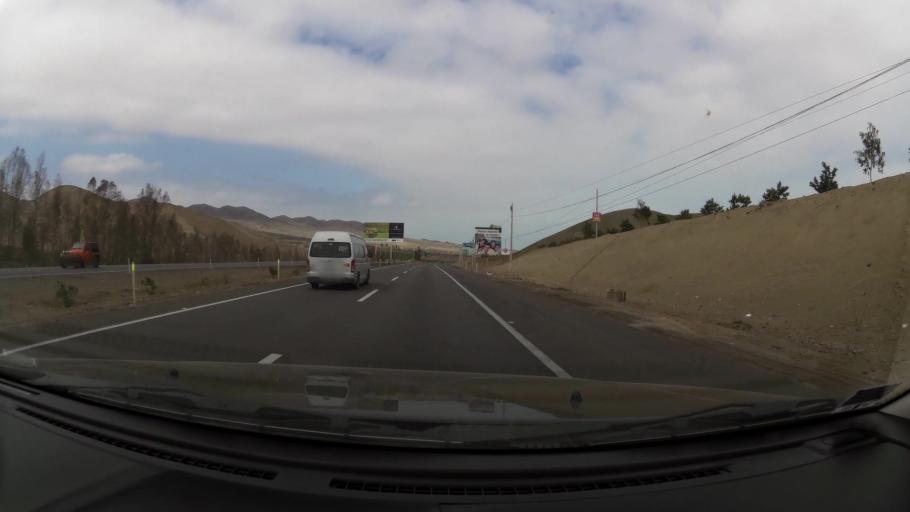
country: PE
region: Lima
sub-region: Provincia de Canete
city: Mala
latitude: -12.5963
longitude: -76.6624
